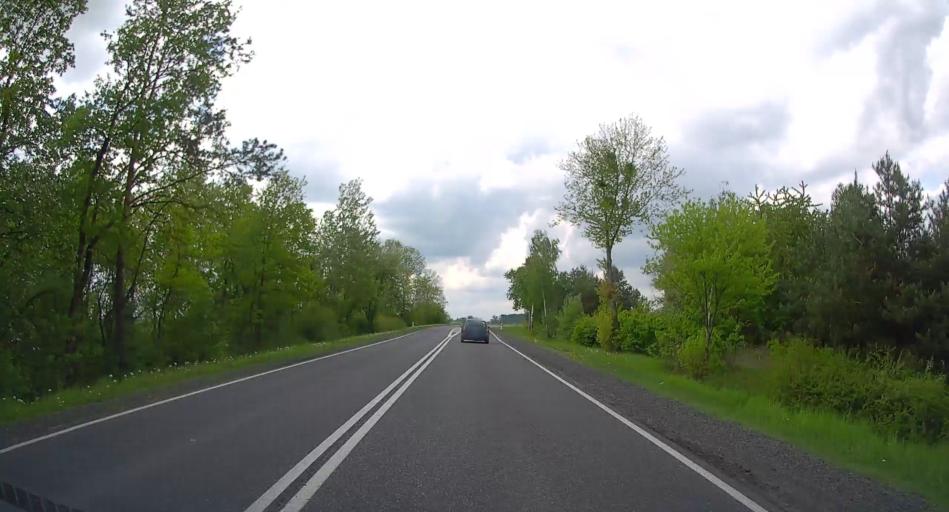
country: PL
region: Masovian Voivodeship
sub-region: Powiat nowodworski
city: Zakroczym
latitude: 52.4434
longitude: 20.5746
